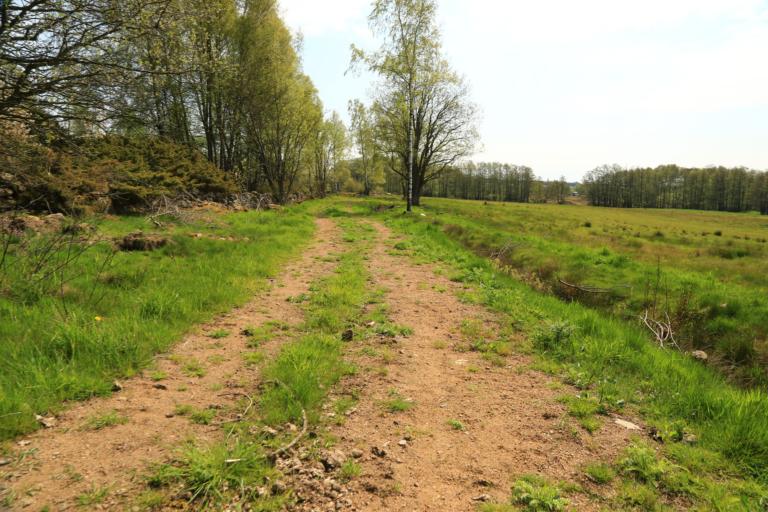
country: SE
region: Halland
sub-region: Varbergs Kommun
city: Varberg
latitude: 57.1301
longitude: 12.2982
